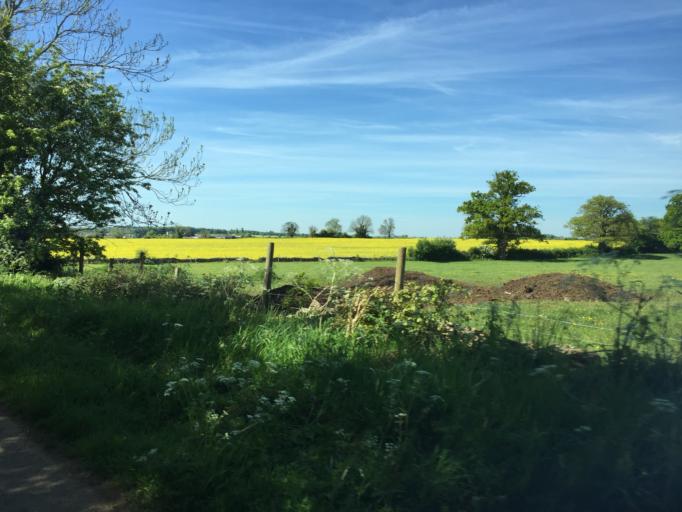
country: GB
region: England
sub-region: Wiltshire
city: Luckington
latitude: 51.6011
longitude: -2.2558
